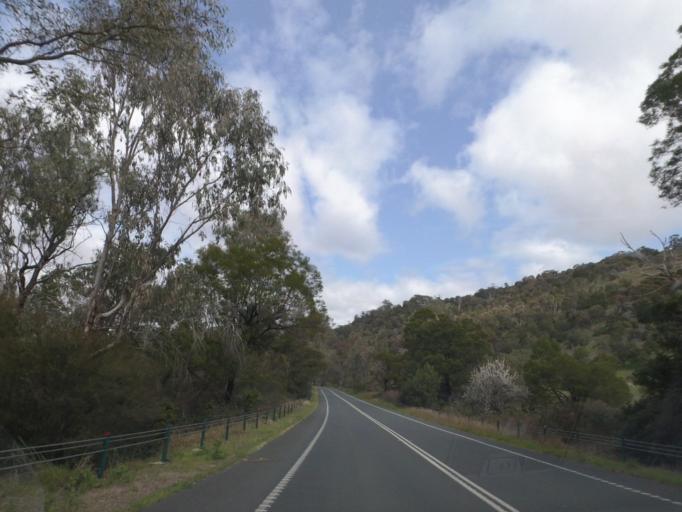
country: AU
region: Victoria
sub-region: Murrindindi
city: Kinglake West
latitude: -37.1082
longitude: 145.2070
